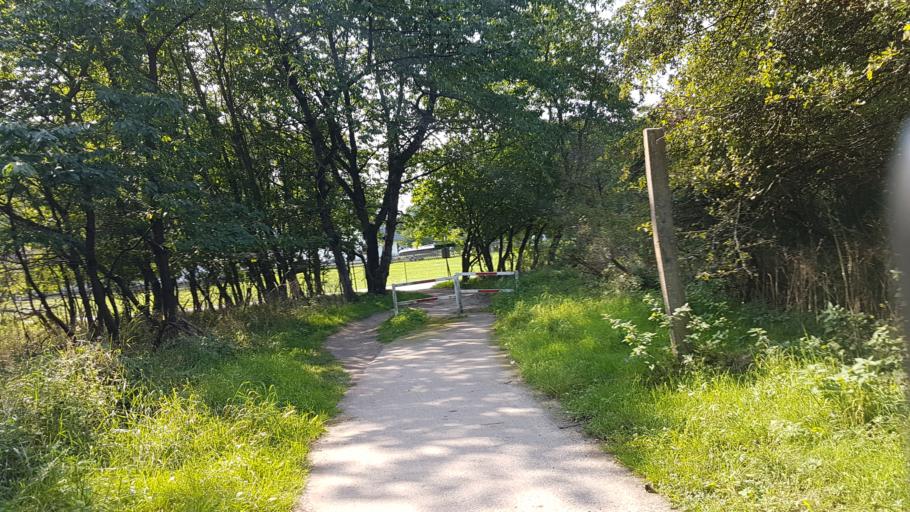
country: DE
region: Mecklenburg-Vorpommern
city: Glowe
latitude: 54.5612
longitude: 13.4858
